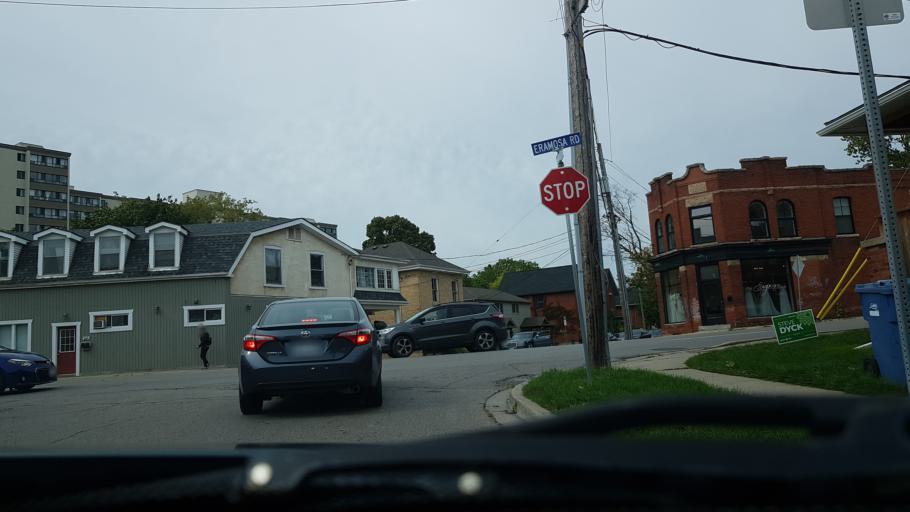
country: CA
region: Ontario
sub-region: Wellington County
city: Guelph
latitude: 43.5495
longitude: -80.2502
